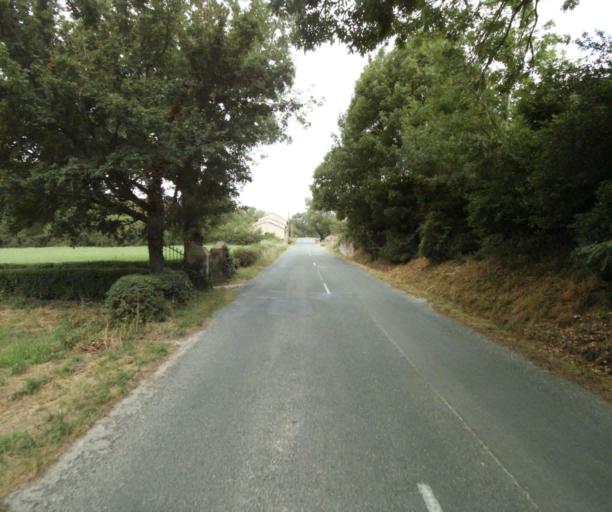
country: FR
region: Midi-Pyrenees
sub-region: Departement du Tarn
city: Soreze
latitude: 43.4494
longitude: 2.0739
